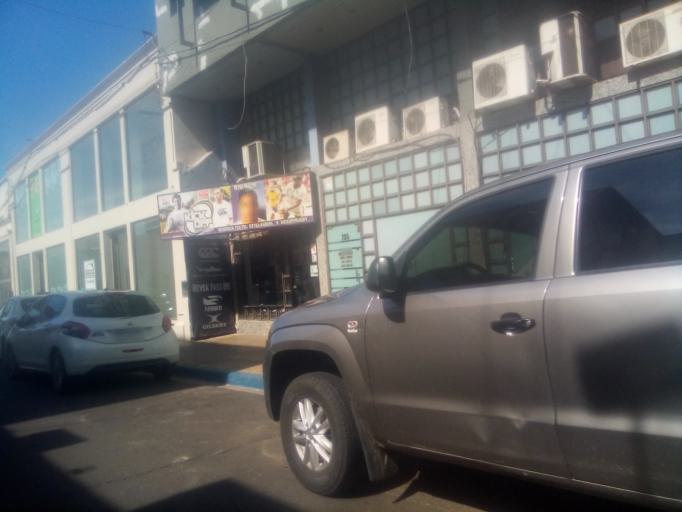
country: AR
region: Corrientes
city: Corrientes
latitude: -27.4659
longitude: -58.8354
